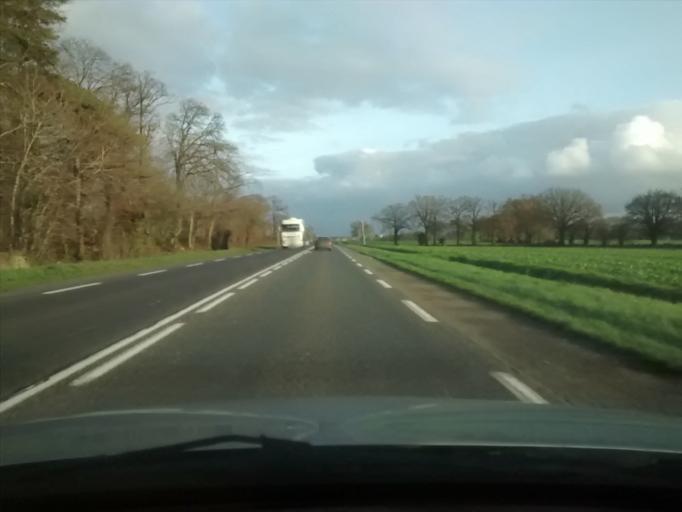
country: FR
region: Pays de la Loire
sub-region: Departement de la Mayenne
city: Saint-Berthevin
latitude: 48.0727
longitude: -0.8686
